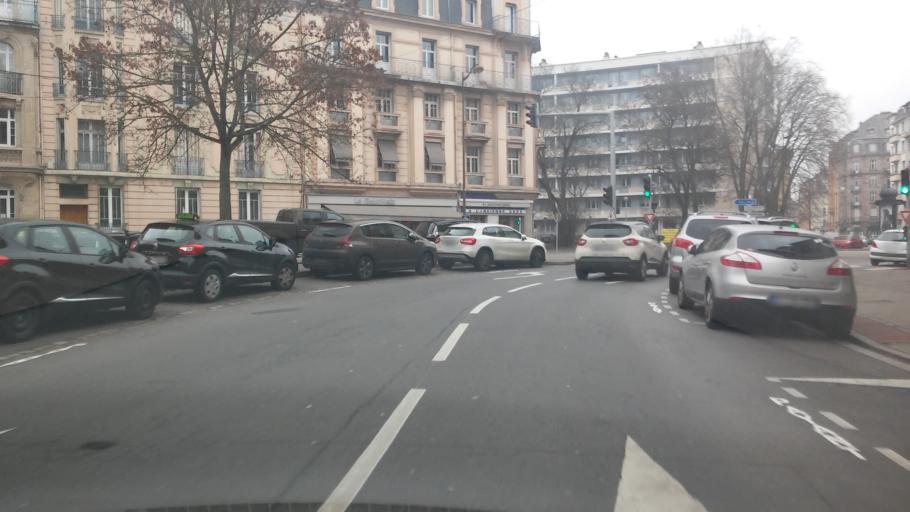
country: FR
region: Lorraine
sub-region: Departement de la Moselle
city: Metz
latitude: 49.1085
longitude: 6.1716
